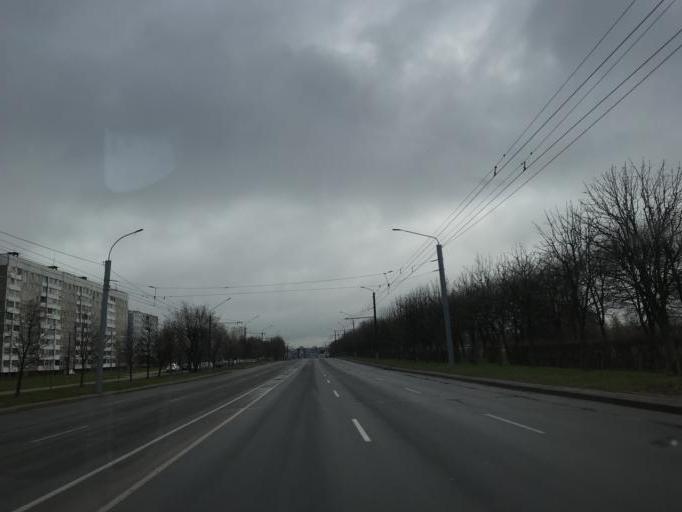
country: BY
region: Mogilev
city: Mahilyow
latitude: 53.8651
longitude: 30.3319
